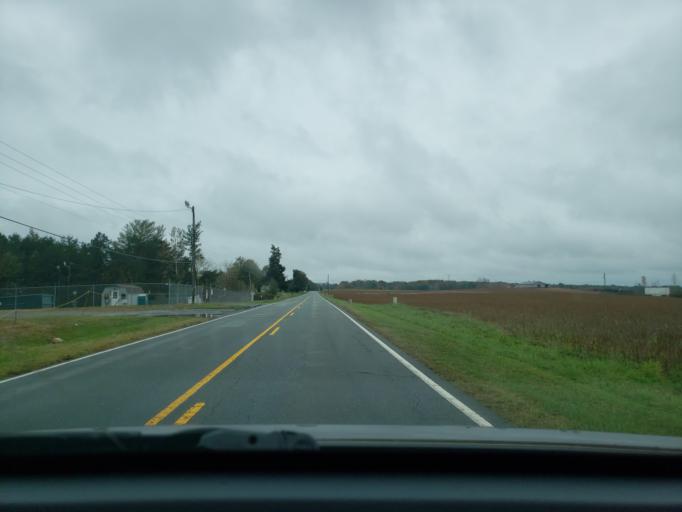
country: US
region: North Carolina
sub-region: Stokes County
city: Walnut Cove
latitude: 36.3334
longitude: -80.1490
